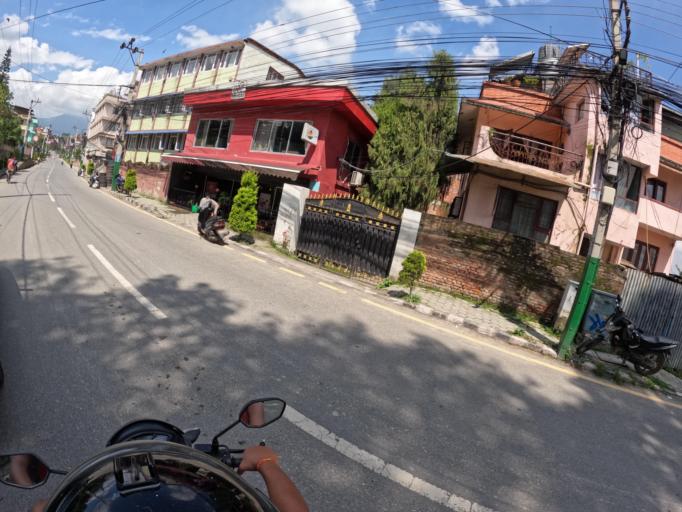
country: NP
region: Central Region
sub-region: Bagmati Zone
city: Patan
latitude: 27.6881
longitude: 85.3088
